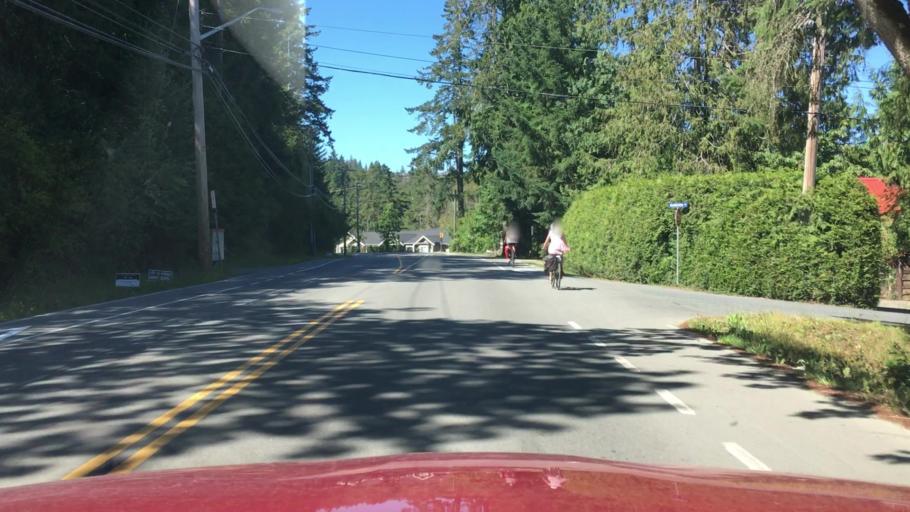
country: CA
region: British Columbia
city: North Saanich
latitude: 48.6737
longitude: -123.4240
